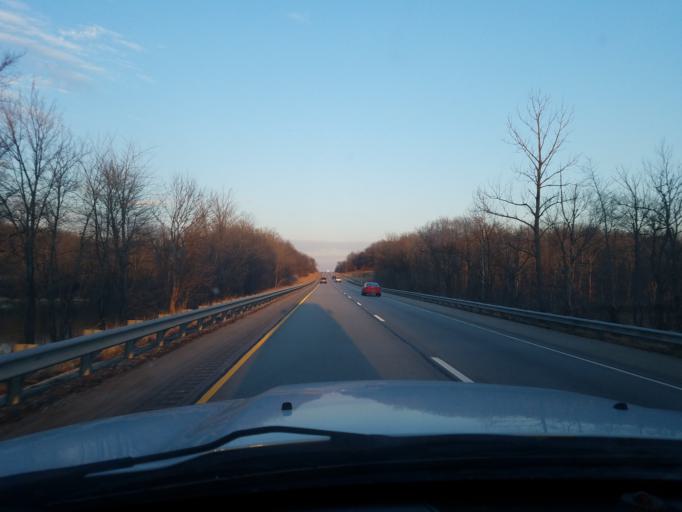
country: US
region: Indiana
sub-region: Warrick County
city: Chandler
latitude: 38.1753
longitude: -87.4133
